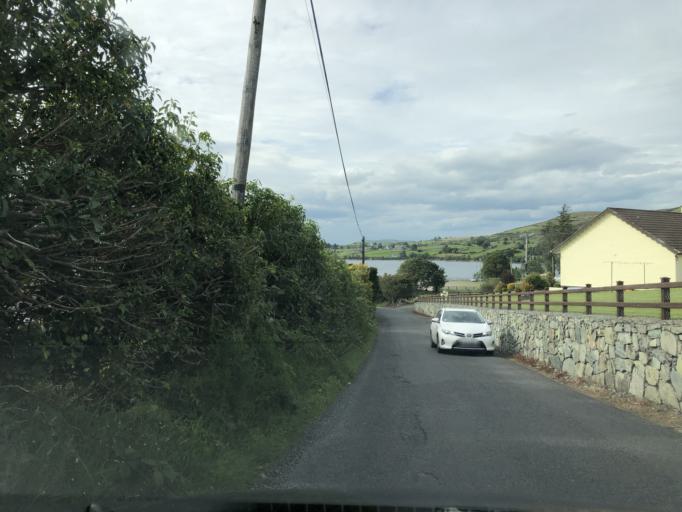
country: GB
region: Northern Ireland
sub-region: Down District
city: Castlewellan
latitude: 54.2331
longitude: -6.0119
